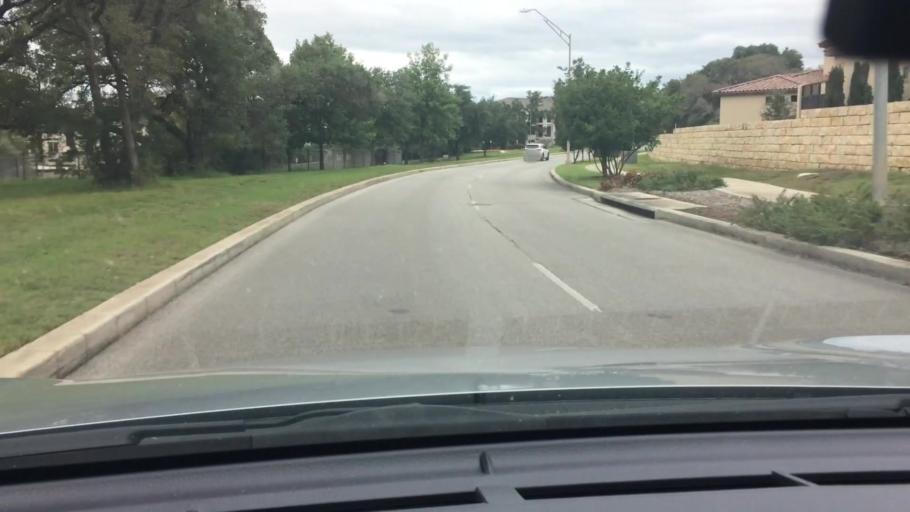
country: US
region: Texas
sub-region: Bexar County
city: Timberwood Park
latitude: 29.6482
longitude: -98.4018
